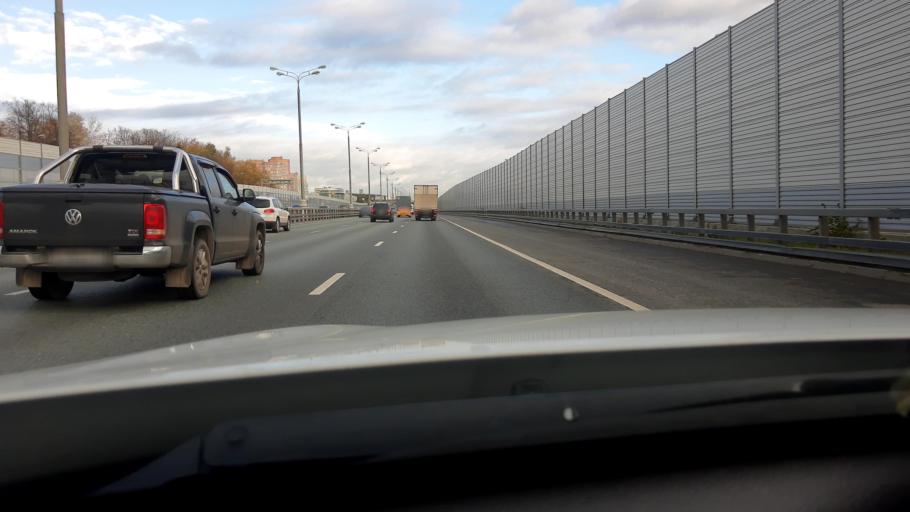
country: RU
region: Moskovskaya
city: Aprelevka
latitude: 55.5361
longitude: 37.0692
